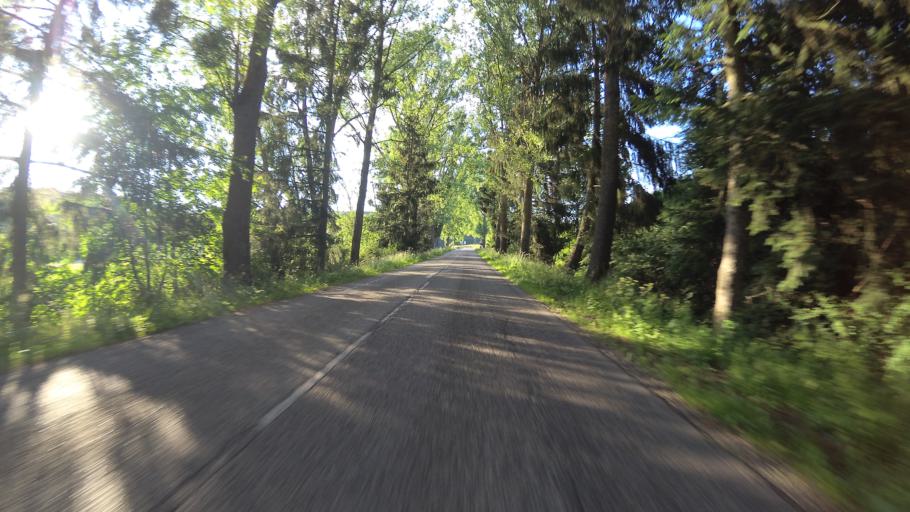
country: FR
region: Alsace
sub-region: Departement du Bas-Rhin
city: Oermingen
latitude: 48.9665
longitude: 7.1377
